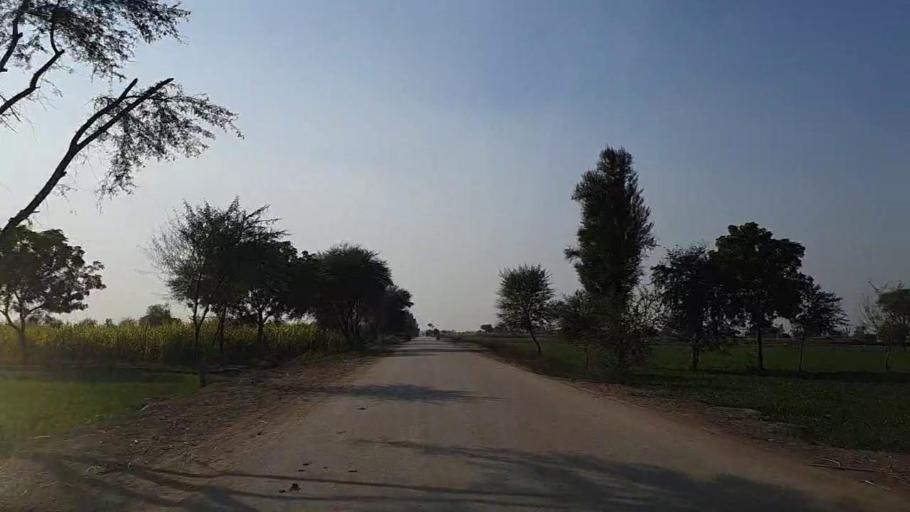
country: PK
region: Sindh
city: Daur
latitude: 26.4039
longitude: 68.2833
